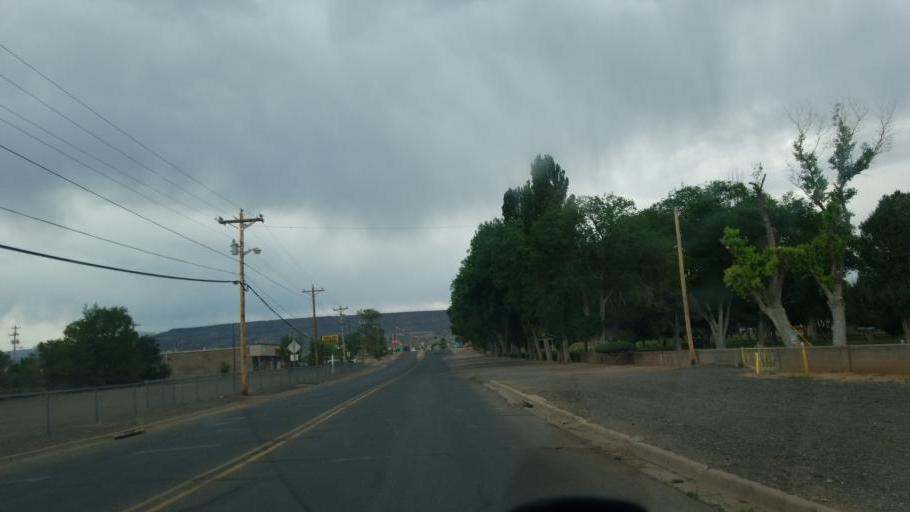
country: US
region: New Mexico
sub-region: Cibola County
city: Grants
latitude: 35.1612
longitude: -107.8376
